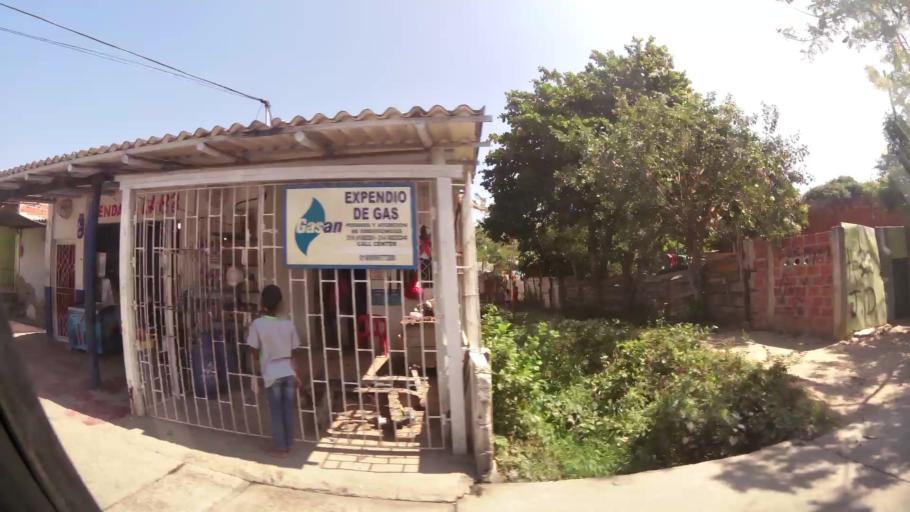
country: CO
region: Atlantico
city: Barranquilla
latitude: 10.9745
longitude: -74.8243
